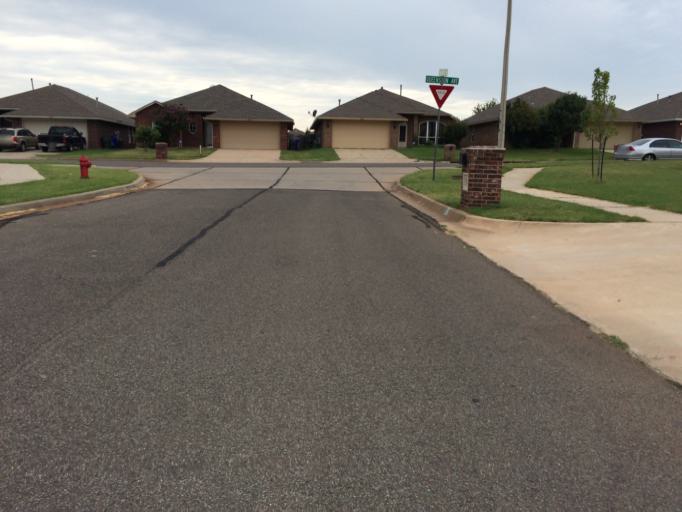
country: US
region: Oklahoma
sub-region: Cleveland County
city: Hall Park
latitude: 35.2499
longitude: -97.4186
